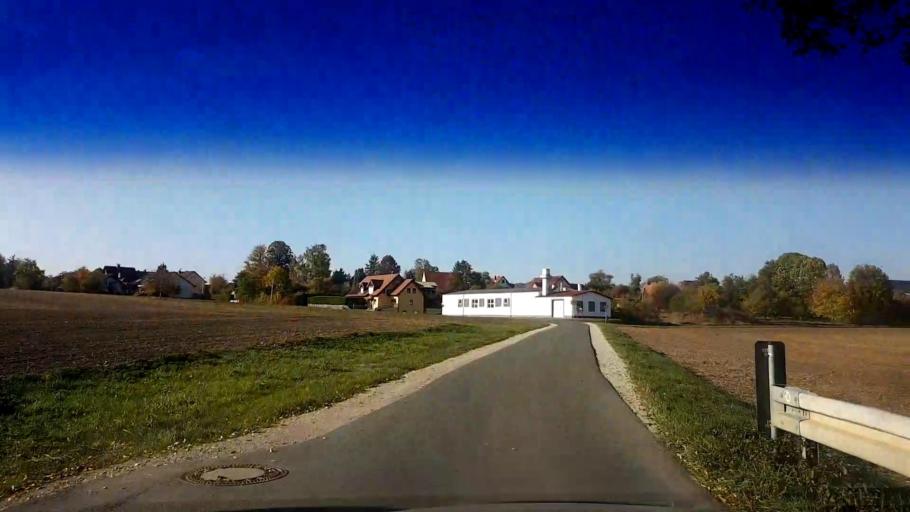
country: DE
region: Bavaria
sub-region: Upper Franconia
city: Strullendorf
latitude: 49.8633
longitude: 10.9973
